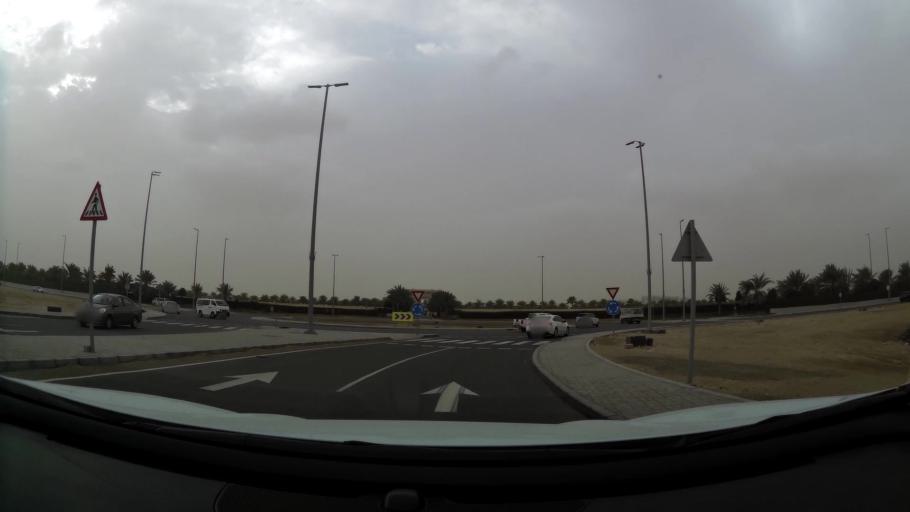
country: AE
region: Abu Dhabi
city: Abu Dhabi
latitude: 24.4253
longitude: 54.5384
